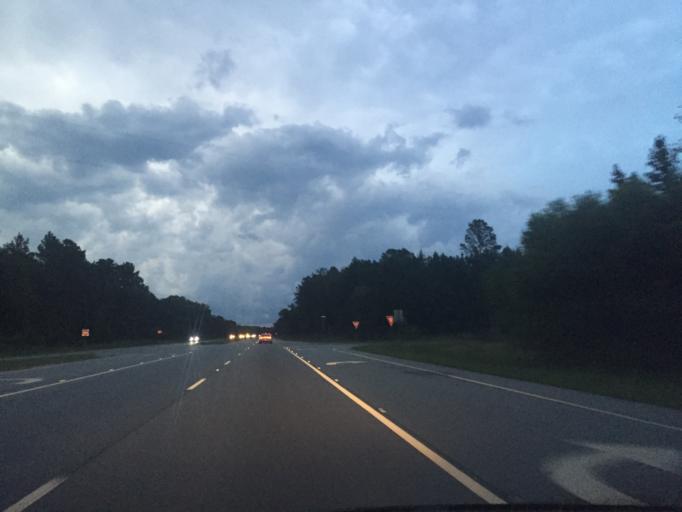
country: US
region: Georgia
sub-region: Liberty County
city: Midway
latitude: 31.8583
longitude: -81.4463
